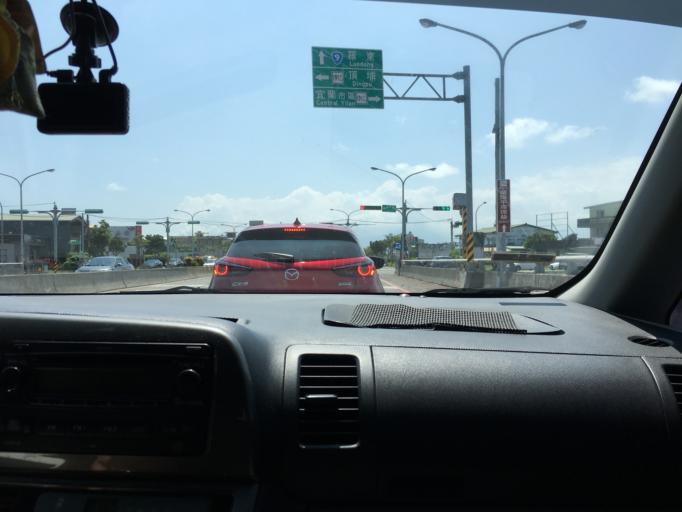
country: TW
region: Taiwan
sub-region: Yilan
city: Yilan
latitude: 24.7572
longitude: 121.7714
